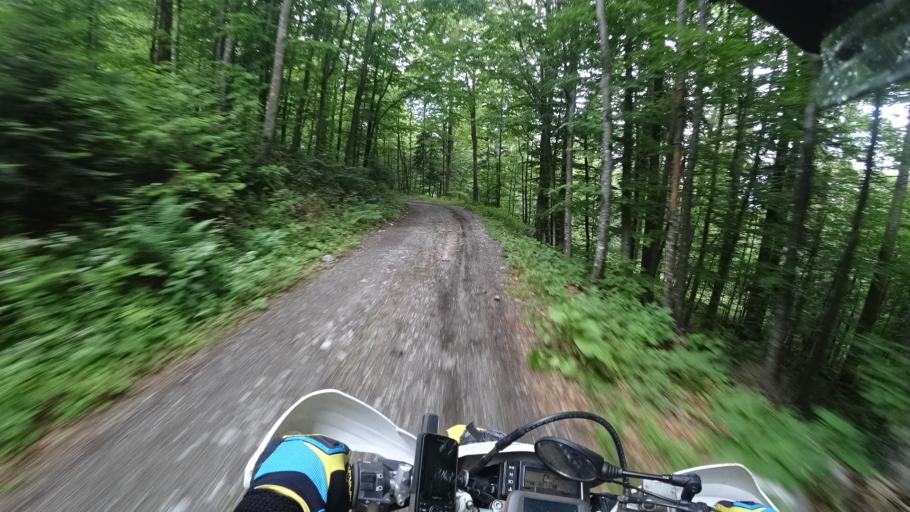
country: HR
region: Primorsko-Goranska
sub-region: Grad Delnice
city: Delnice
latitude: 45.3085
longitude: 14.7621
